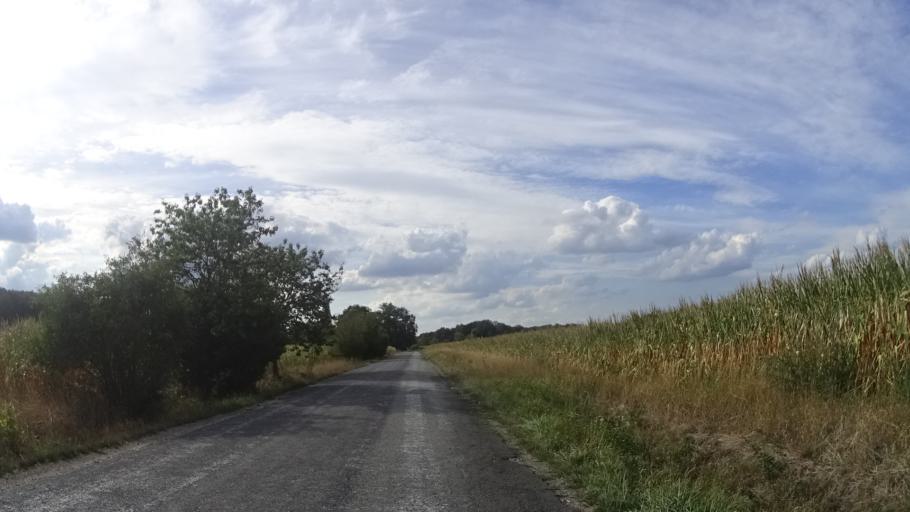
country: CZ
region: Olomoucky
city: Dubicko
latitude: 49.7986
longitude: 16.9567
